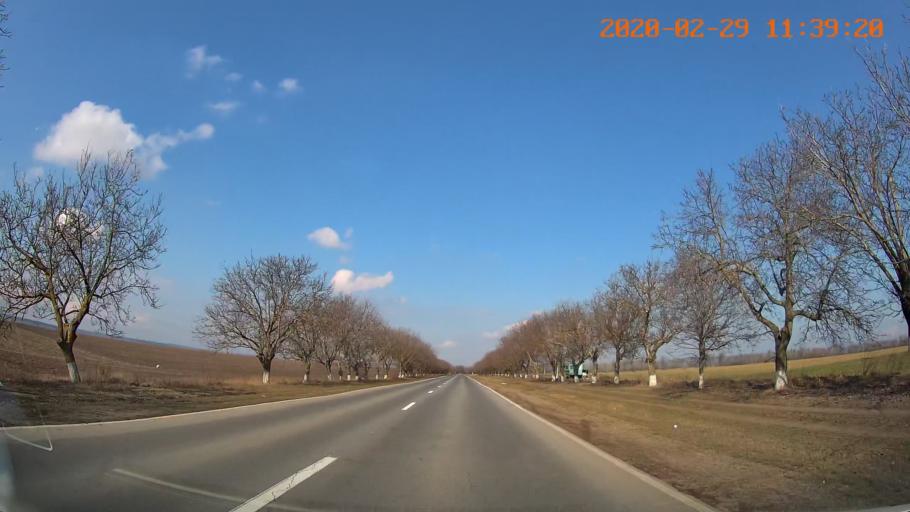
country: MD
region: Rezina
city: Saharna
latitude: 47.6387
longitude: 29.0264
